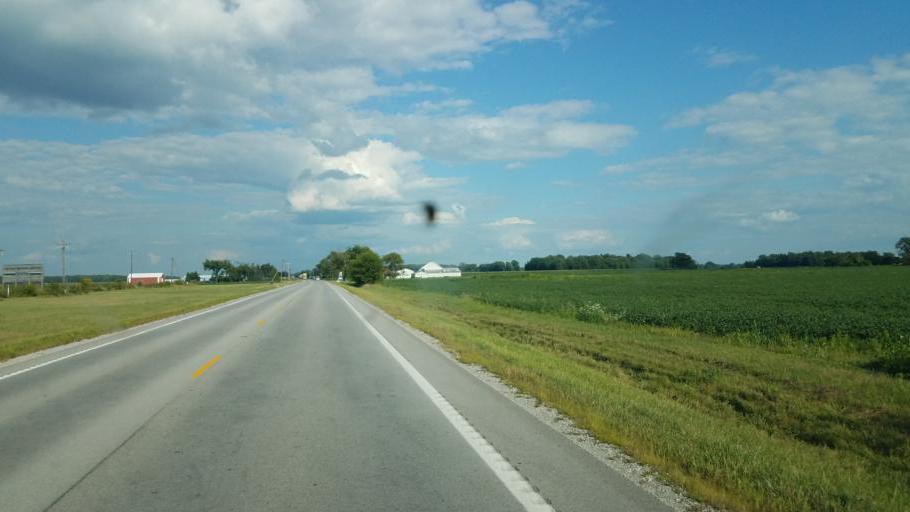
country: US
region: Ohio
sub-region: Wood County
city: Bowling Green
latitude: 41.3621
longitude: -83.5613
